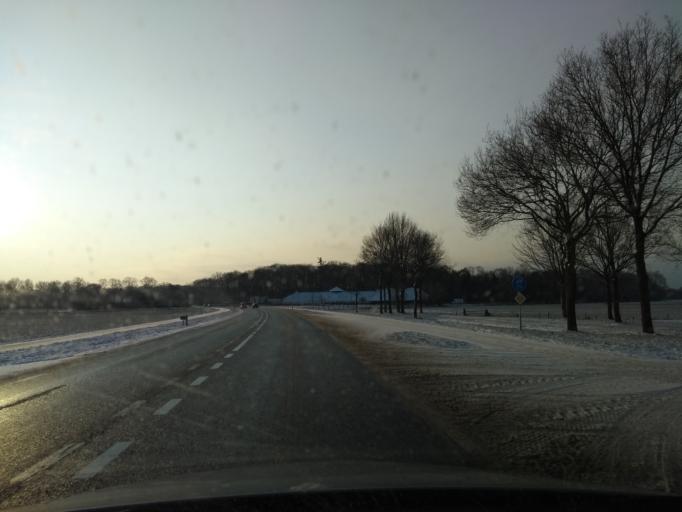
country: NL
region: Overijssel
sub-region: Gemeente Hof van Twente
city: Delden
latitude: 52.2922
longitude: 6.6628
